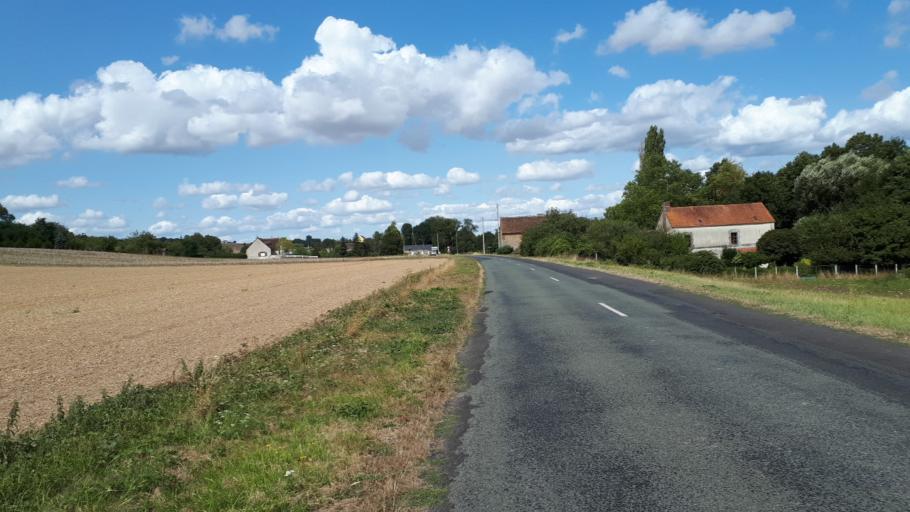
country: FR
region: Centre
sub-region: Departement du Loir-et-Cher
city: Aze
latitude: 47.8378
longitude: 0.9878
